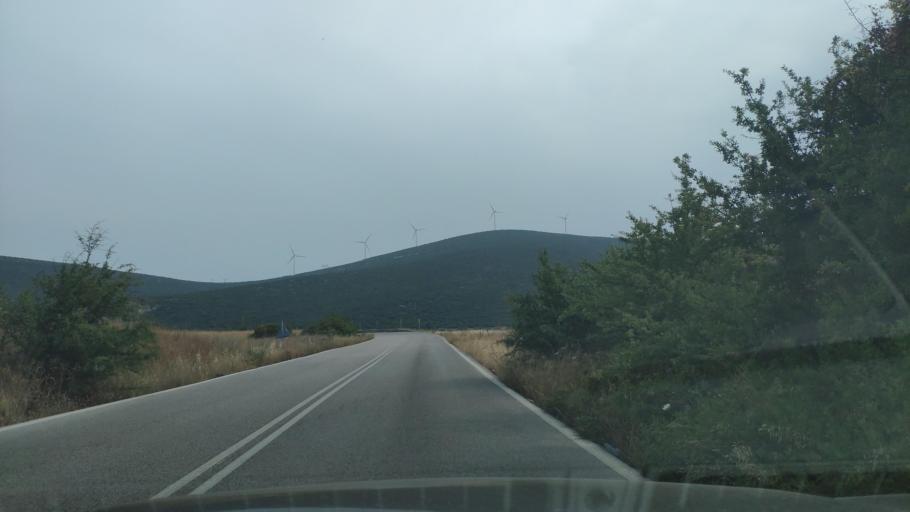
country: GR
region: Peloponnese
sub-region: Nomos Argolidos
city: Didyma
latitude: 37.5136
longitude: 23.1762
